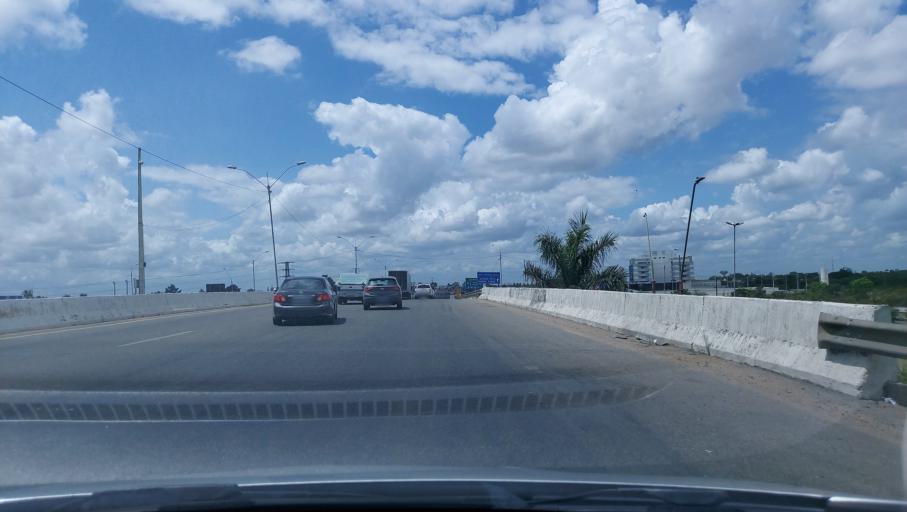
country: BR
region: Bahia
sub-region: Feira De Santana
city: Feira de Santana
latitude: -12.2718
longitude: -38.9358
